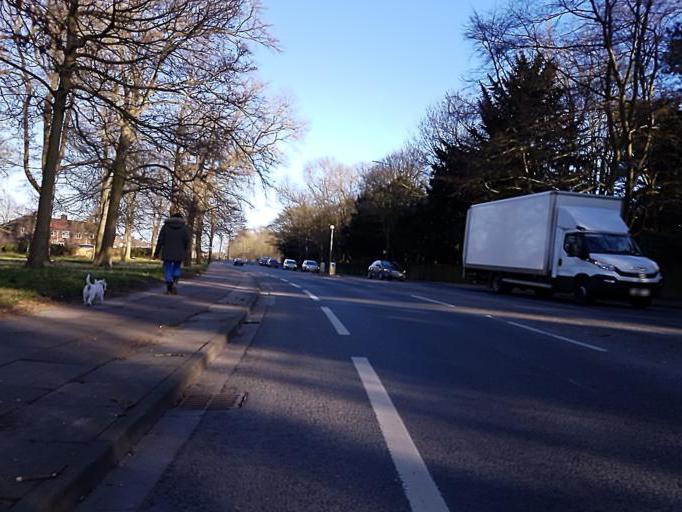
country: GB
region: England
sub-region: North East Lincolnshire
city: Grimsby
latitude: 53.5533
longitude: -0.0691
